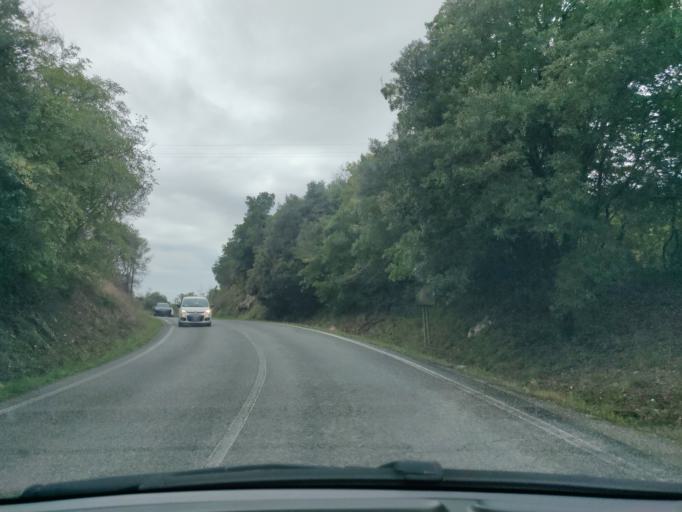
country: IT
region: Latium
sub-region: Citta metropolitana di Roma Capitale
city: Allumiere
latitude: 42.1381
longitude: 11.8714
